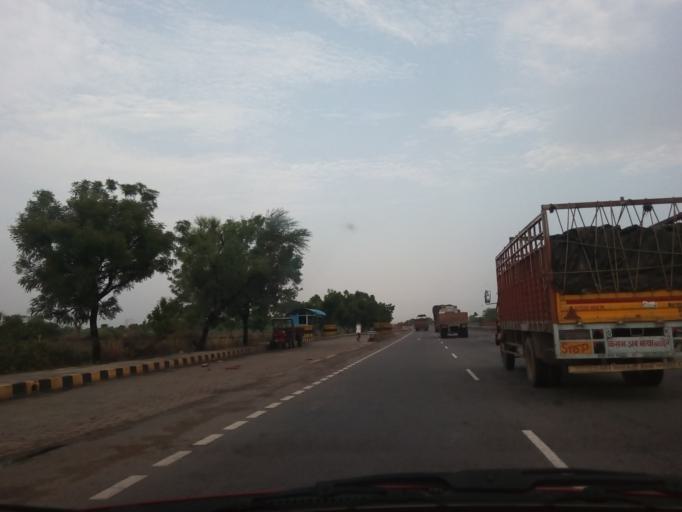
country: IN
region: Rajasthan
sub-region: Jaipur
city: Naraina
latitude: 26.6509
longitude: 75.1344
